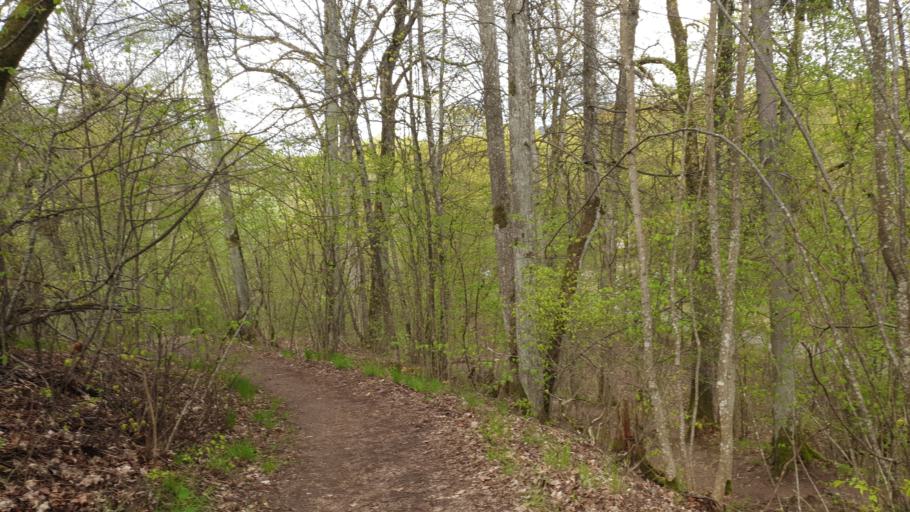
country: LT
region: Kauno apskritis
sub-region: Kauno rajonas
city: Akademija (Kaunas)
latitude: 54.9460
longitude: 23.7859
